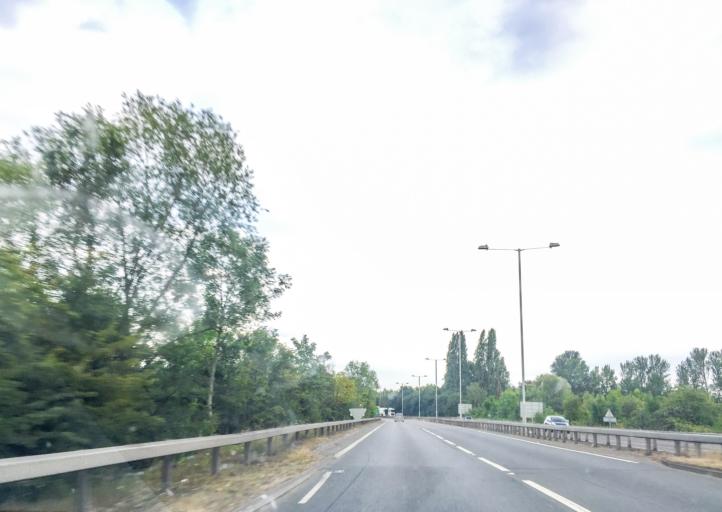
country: GB
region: England
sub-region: Surrey
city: Staines
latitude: 51.4441
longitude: -0.5277
